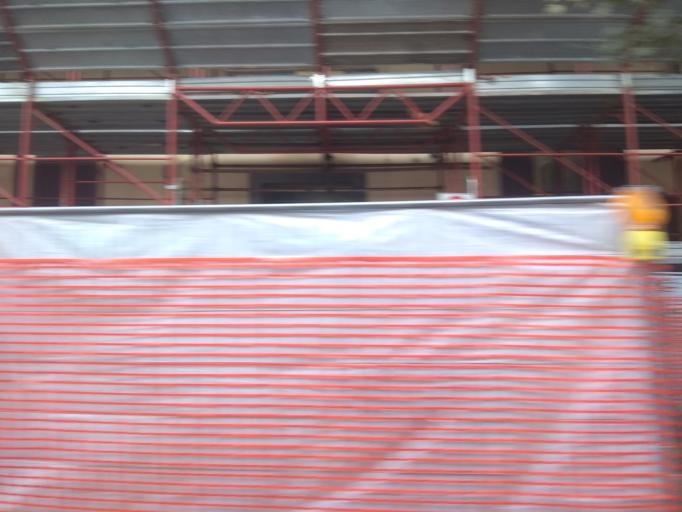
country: IT
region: Latium
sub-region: Citta metropolitana di Roma Capitale
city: Civitavecchia
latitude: 42.0966
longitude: 11.7896
